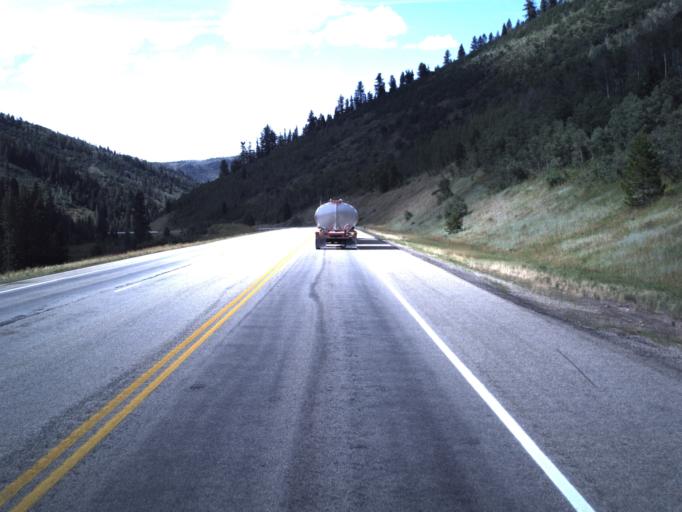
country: US
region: Utah
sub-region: Wasatch County
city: Heber
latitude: 40.3178
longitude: -111.2582
